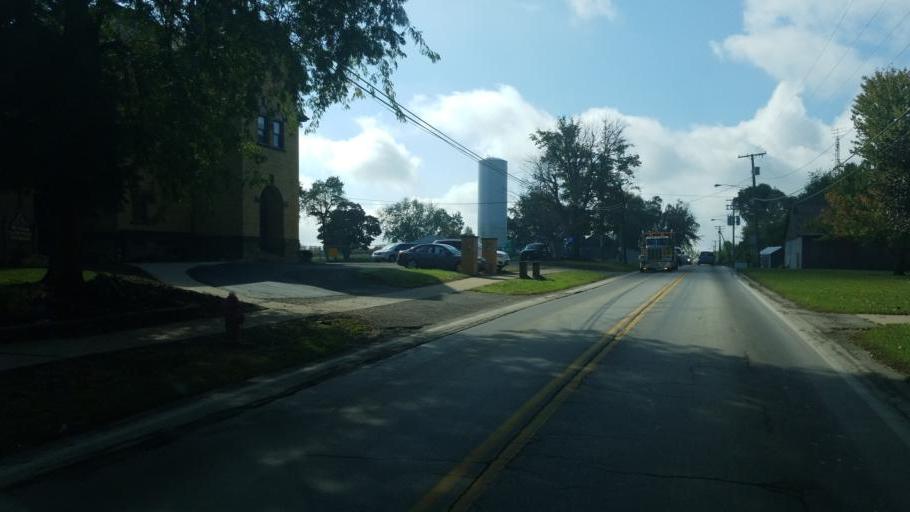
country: US
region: Ohio
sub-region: Wayne County
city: Dalton
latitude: 40.6932
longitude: -81.7037
